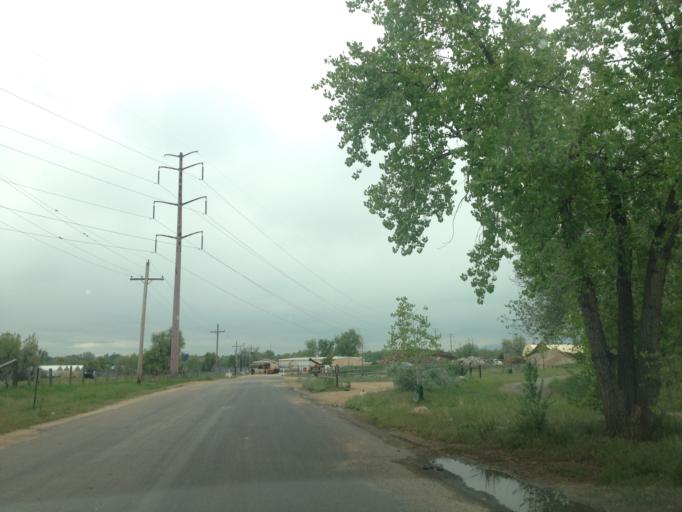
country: US
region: Colorado
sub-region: Boulder County
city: Gunbarrel
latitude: 40.0451
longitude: -105.1833
